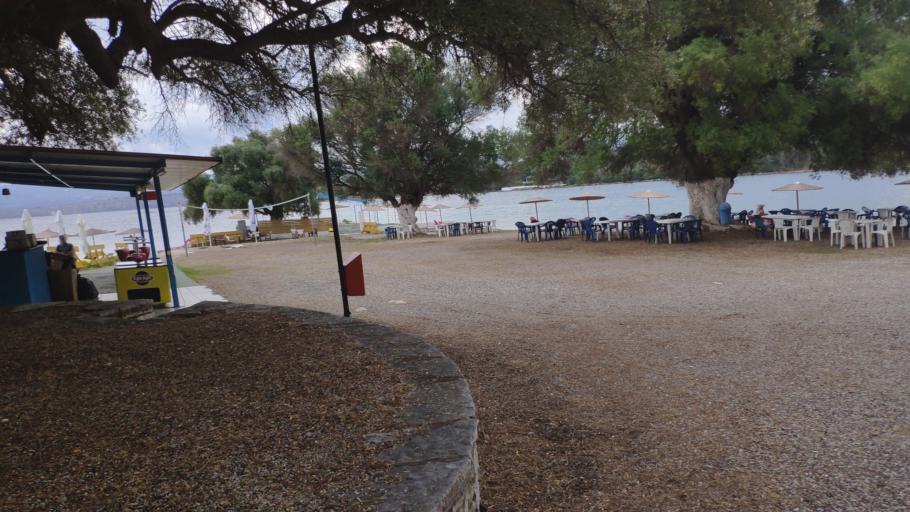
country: GR
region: West Greece
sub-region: Nomos Aitolias kai Akarnanias
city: Amfilochia
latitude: 38.9073
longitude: 21.1146
